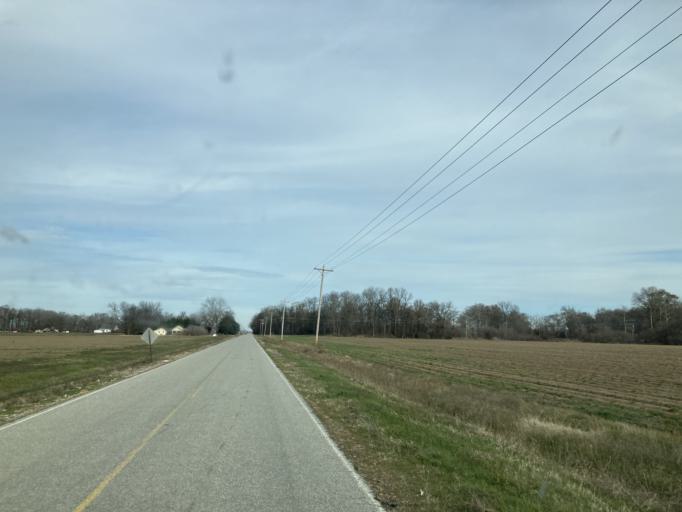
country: US
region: Mississippi
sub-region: Humphreys County
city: Belzoni
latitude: 33.0640
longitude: -90.6155
